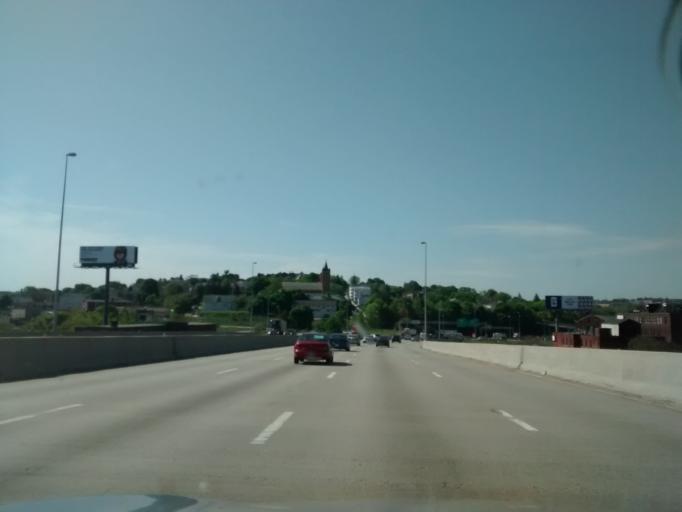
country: US
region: Massachusetts
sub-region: Worcester County
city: Worcester
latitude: 42.2606
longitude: -71.7936
